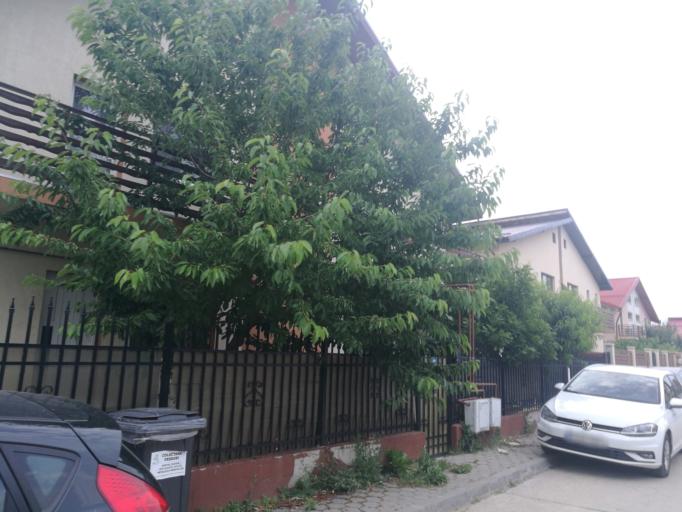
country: RO
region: Ilfov
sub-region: Comuna Vidra
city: Vidra
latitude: 44.2790
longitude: 26.1819
